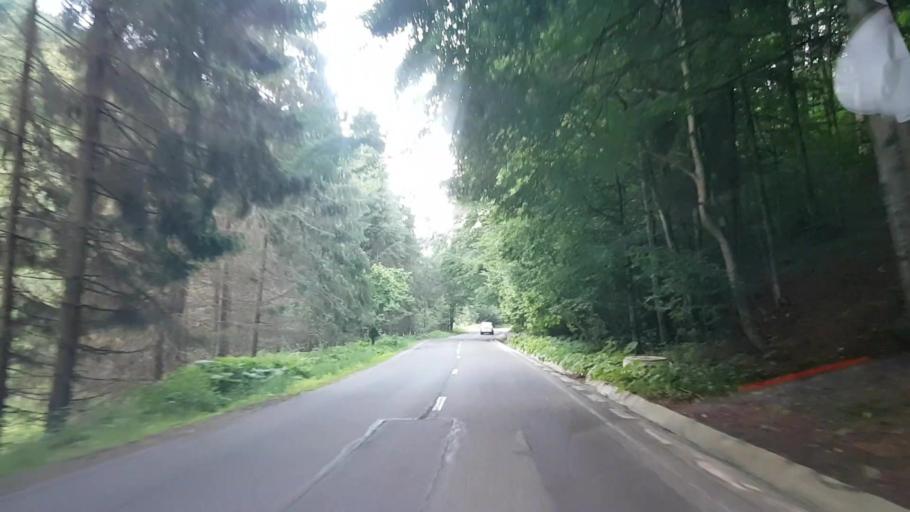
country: RO
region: Harghita
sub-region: Comuna Praid
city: Ocna de Sus
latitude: 46.6056
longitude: 25.2400
